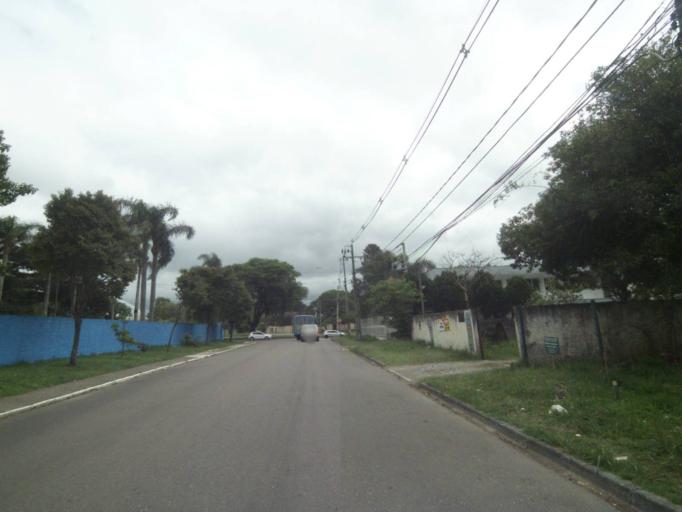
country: BR
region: Parana
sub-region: Pinhais
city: Pinhais
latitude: -25.4300
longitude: -49.2214
